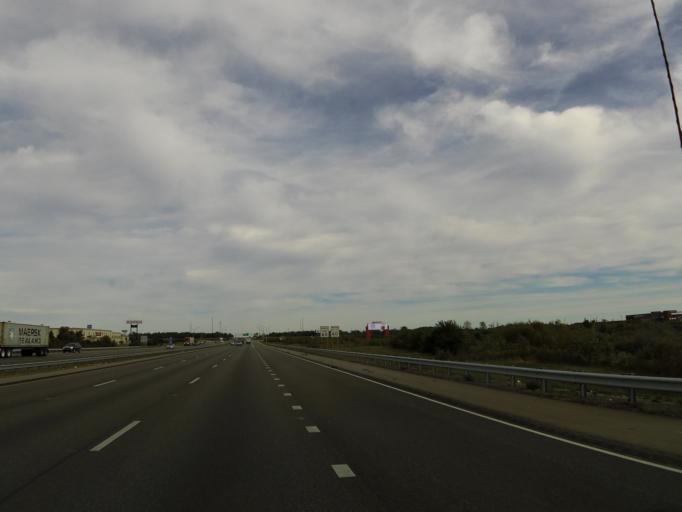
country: US
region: Indiana
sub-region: Johnson County
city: Greenwood
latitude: 39.6262
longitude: -86.0740
